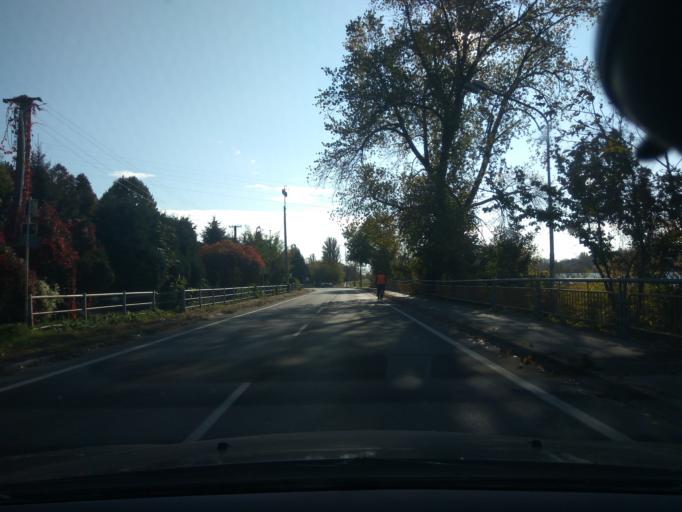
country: SK
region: Trnavsky
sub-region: Okres Trnava
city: Piestany
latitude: 48.5806
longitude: 17.8355
